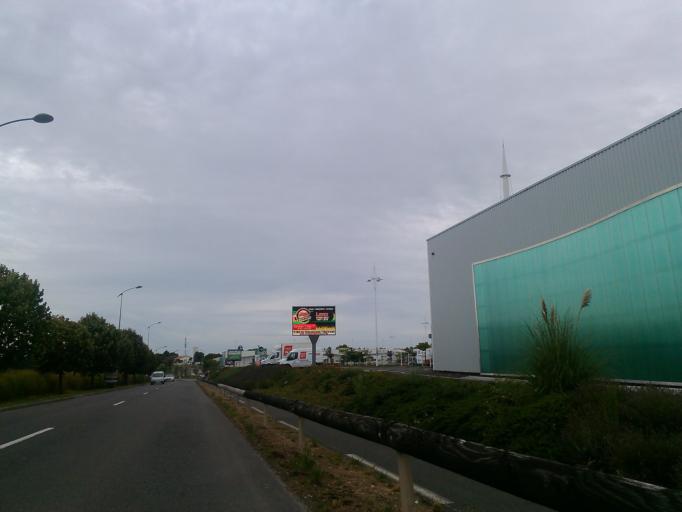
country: FR
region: Poitou-Charentes
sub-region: Departement de la Charente-Maritime
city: Vaux-sur-Mer
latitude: 45.6474
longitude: -1.0495
